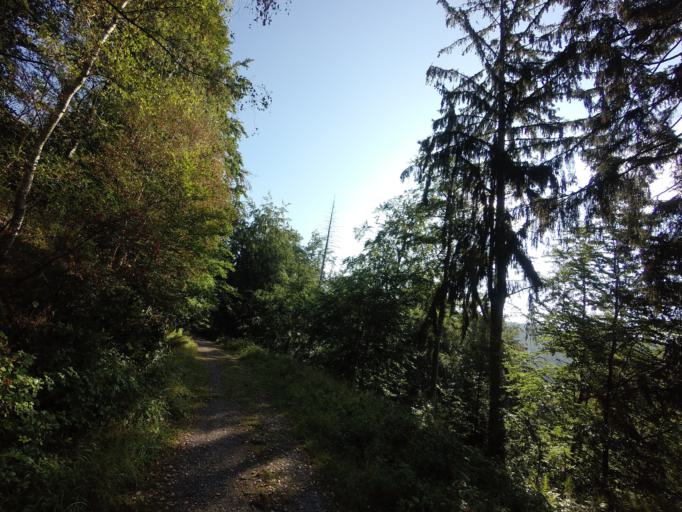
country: DE
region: North Rhine-Westphalia
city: Heimbach
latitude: 50.6133
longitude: 6.4042
